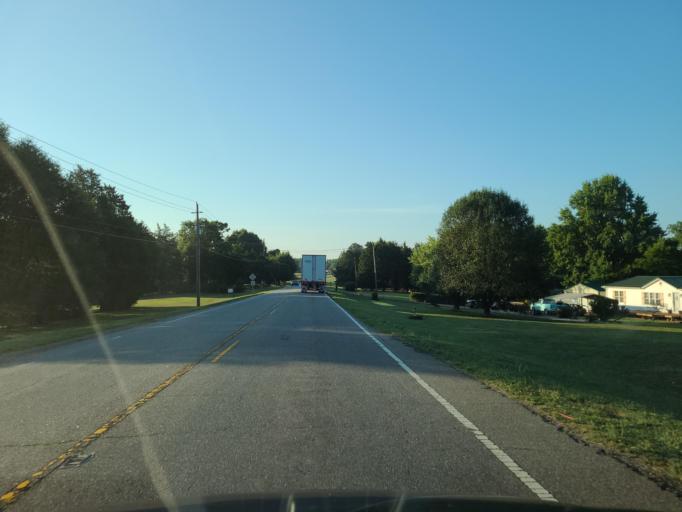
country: US
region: North Carolina
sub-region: Catawba County
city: Mountain View
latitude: 35.6309
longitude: -81.3791
